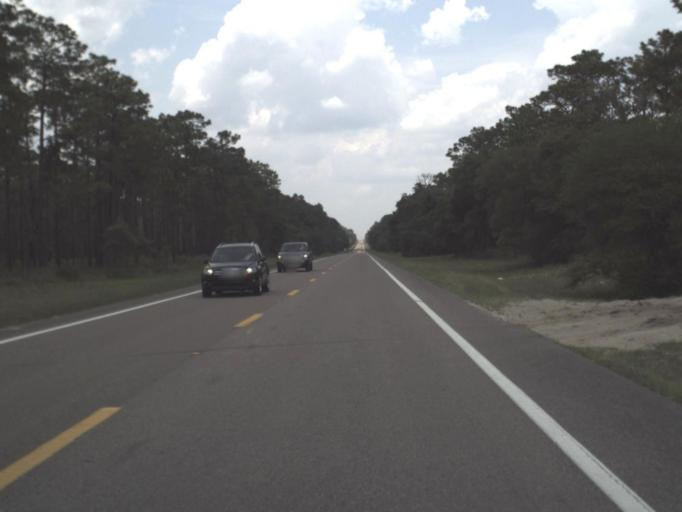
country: US
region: Florida
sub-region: Putnam County
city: Crescent City
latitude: 29.4094
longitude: -81.7369
